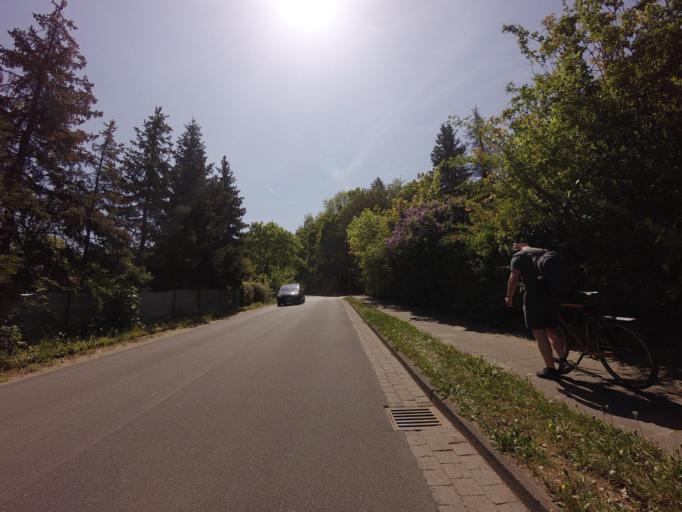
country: DE
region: Lower Saxony
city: Hildesheim
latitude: 52.1462
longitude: 9.9731
